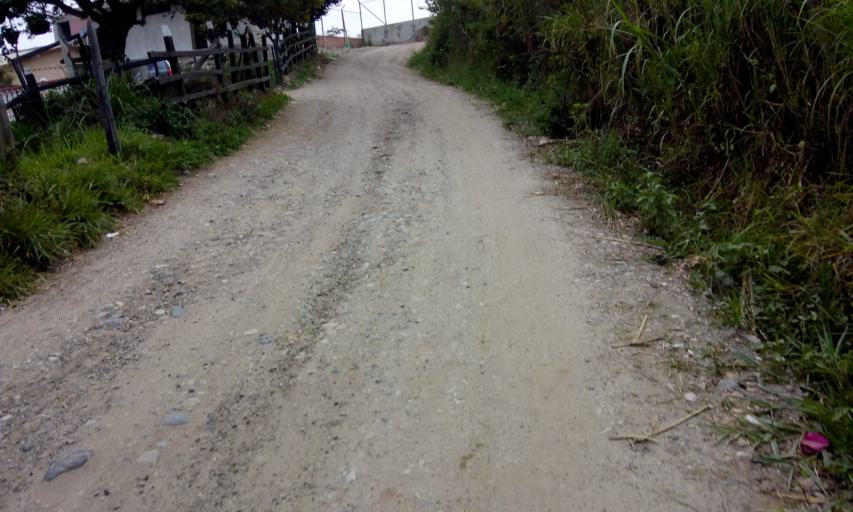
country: CO
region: Boyaca
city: Tipacoque
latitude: 6.4137
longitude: -72.6882
